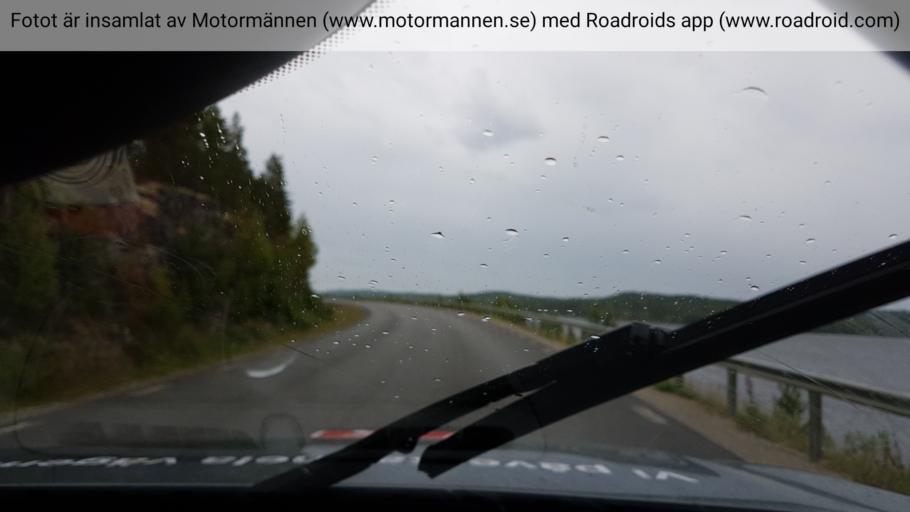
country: SE
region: Jaemtland
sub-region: Braecke Kommun
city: Braecke
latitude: 62.3982
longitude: 15.0294
